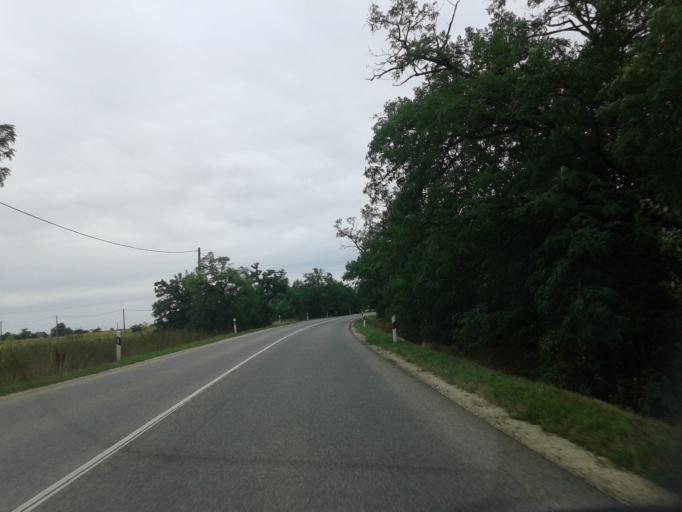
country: HU
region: Pest
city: Dunavarsany
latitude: 47.2718
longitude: 19.0313
